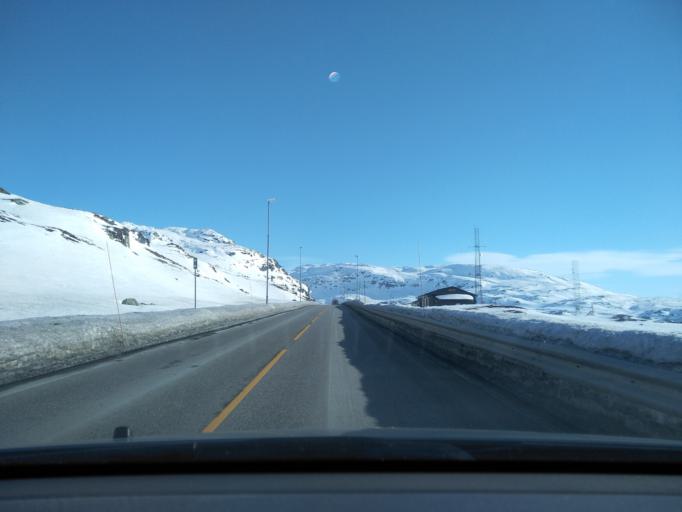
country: NO
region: Aust-Agder
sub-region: Bykle
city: Hovden
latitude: 59.8412
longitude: 6.9814
